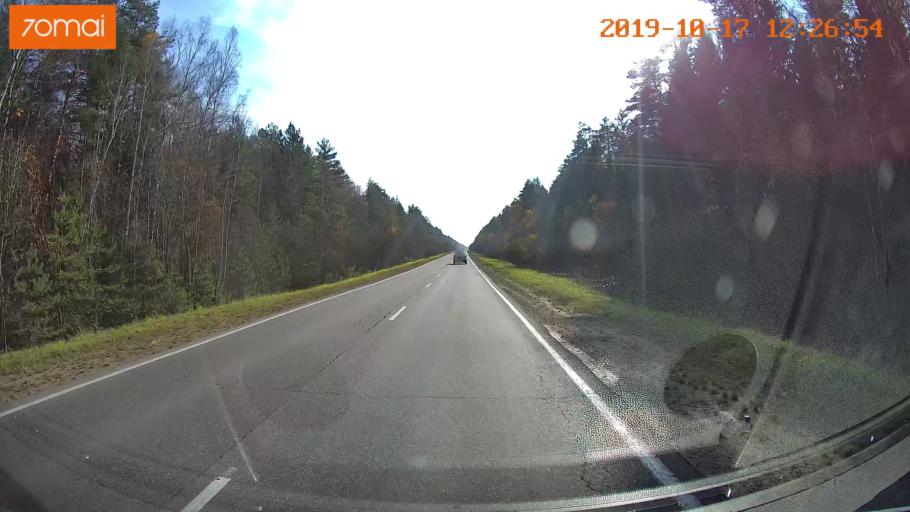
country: RU
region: Rjazan
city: Syntul
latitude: 55.0128
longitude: 41.2591
